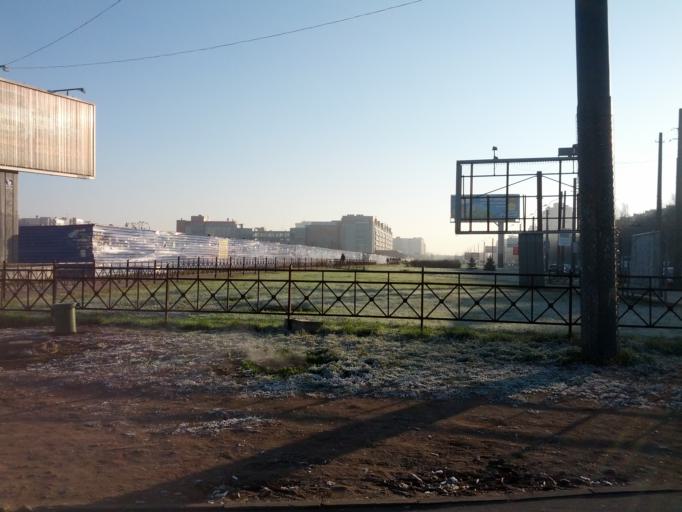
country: RU
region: St.-Petersburg
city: Krasnogvargeisky
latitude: 59.9068
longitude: 30.4833
